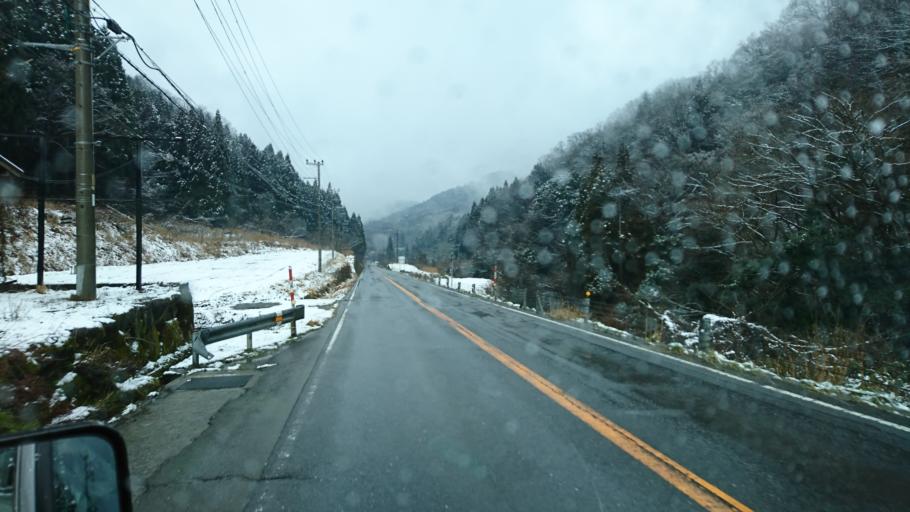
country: JP
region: Tottori
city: Tottori
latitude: 35.5288
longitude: 134.5176
